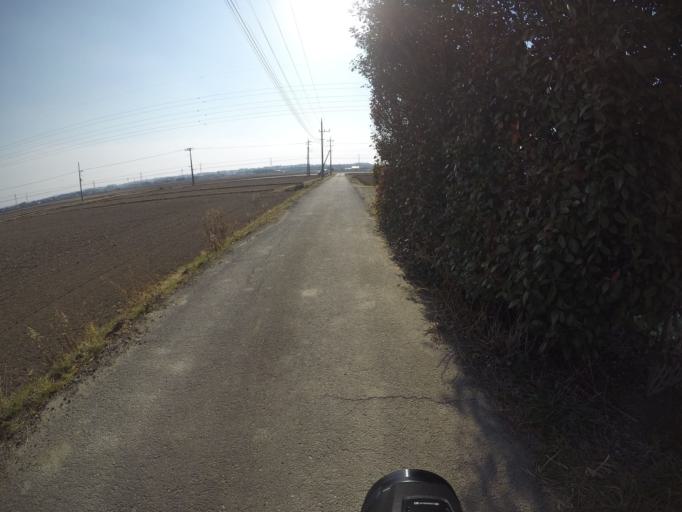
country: JP
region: Ibaraki
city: Tsukuba
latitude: 36.1512
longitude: 140.1220
